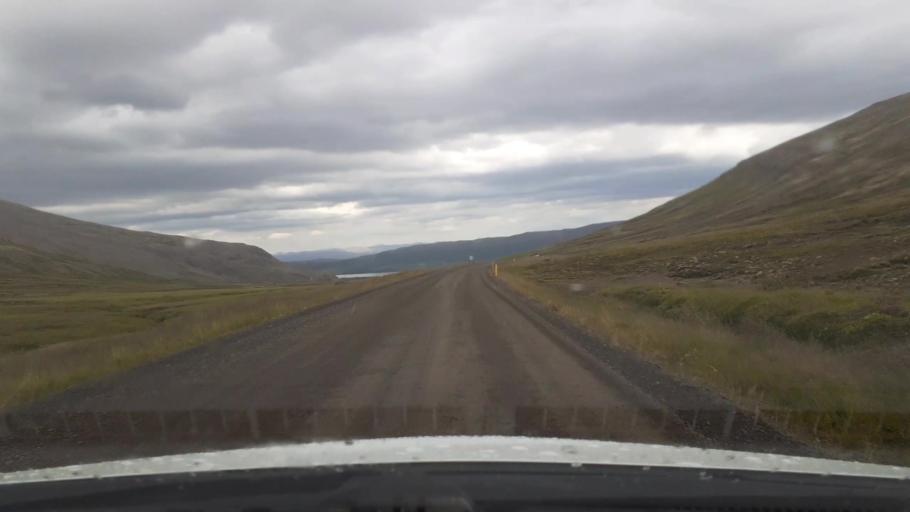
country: IS
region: Capital Region
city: Mosfellsbaer
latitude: 64.4952
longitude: -21.5262
